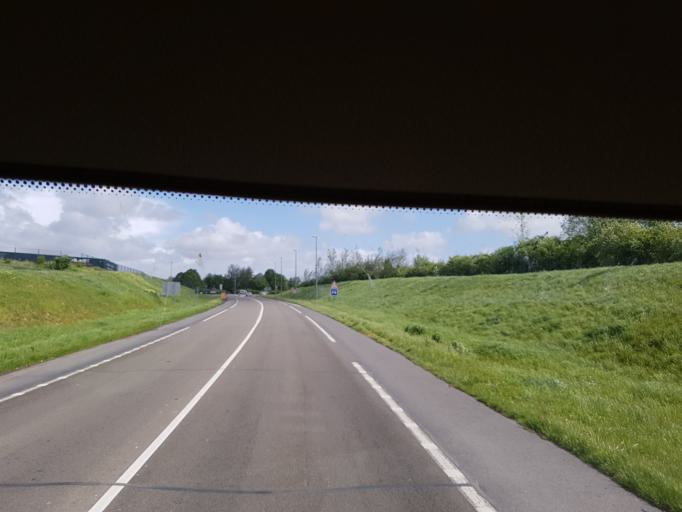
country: FR
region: Nord-Pas-de-Calais
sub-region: Departement du Nord
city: Proville
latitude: 50.1726
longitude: 3.1960
